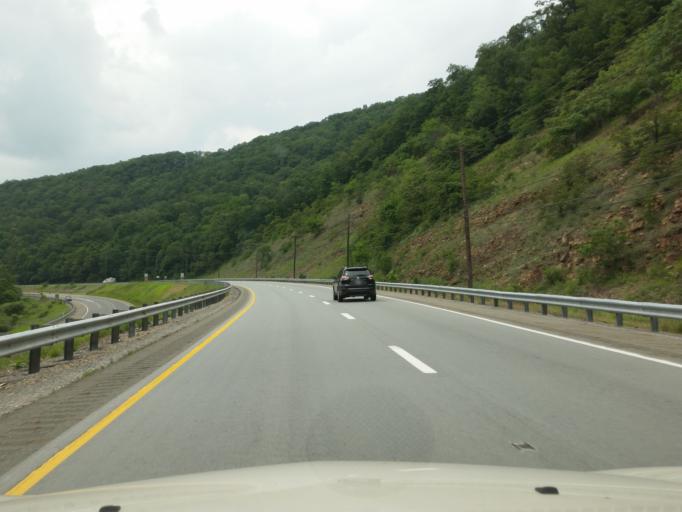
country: US
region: Pennsylvania
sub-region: Perry County
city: Newport
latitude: 40.5634
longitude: -77.1681
